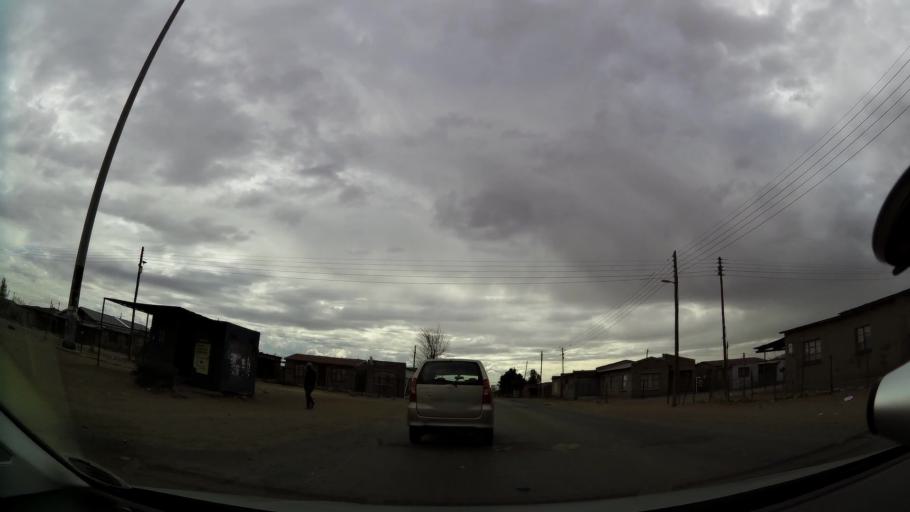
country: ZA
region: Orange Free State
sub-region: Fezile Dabi District Municipality
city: Kroonstad
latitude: -27.6484
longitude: 27.1964
